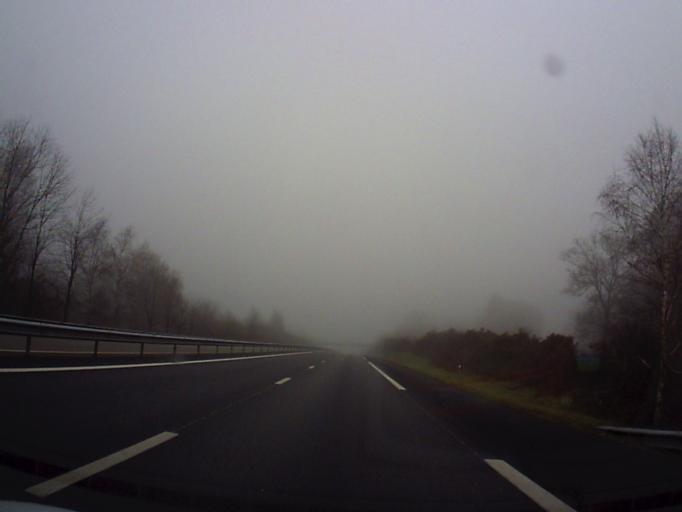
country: FR
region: Brittany
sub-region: Departement du Morbihan
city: Augan
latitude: 47.9277
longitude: -2.2422
